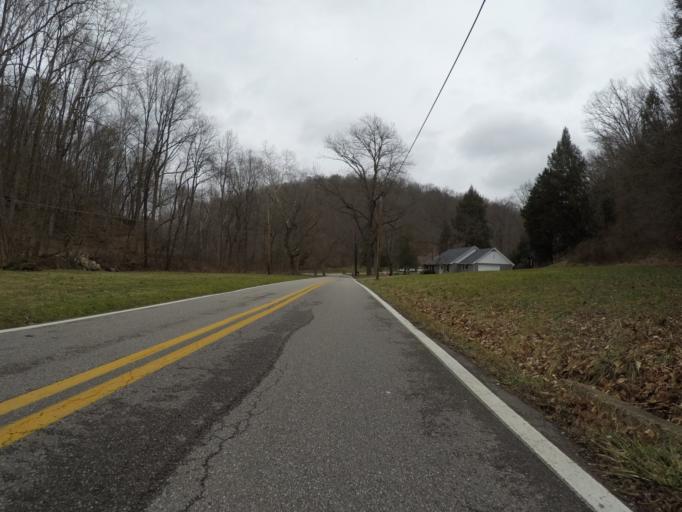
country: US
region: West Virginia
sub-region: Cabell County
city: Barboursville
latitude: 38.4444
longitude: -82.2462
